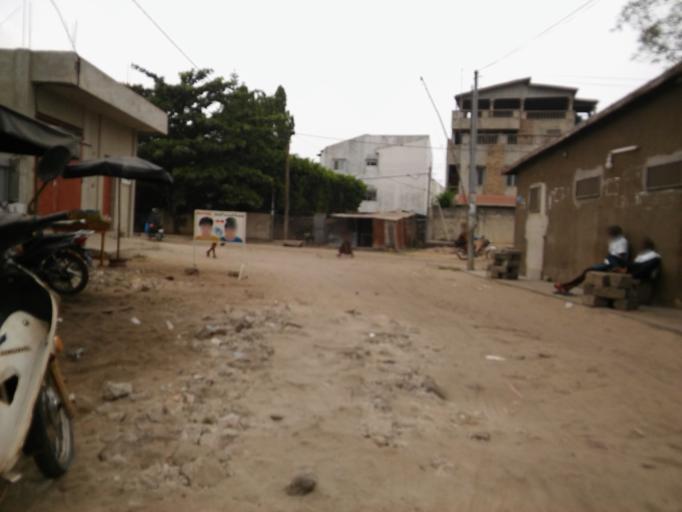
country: BJ
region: Littoral
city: Cotonou
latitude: 6.3917
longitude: 2.3722
